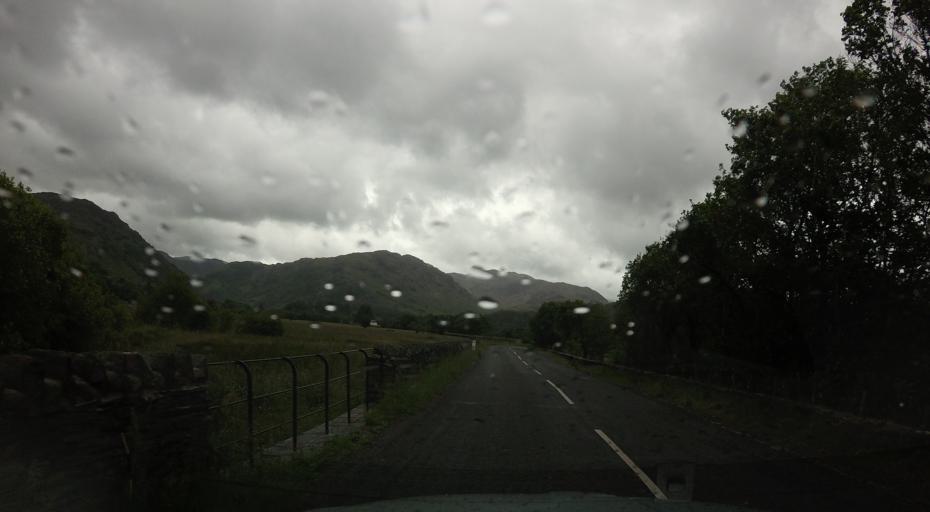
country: GB
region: England
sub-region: Cumbria
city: Keswick
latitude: 54.5317
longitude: -3.1511
